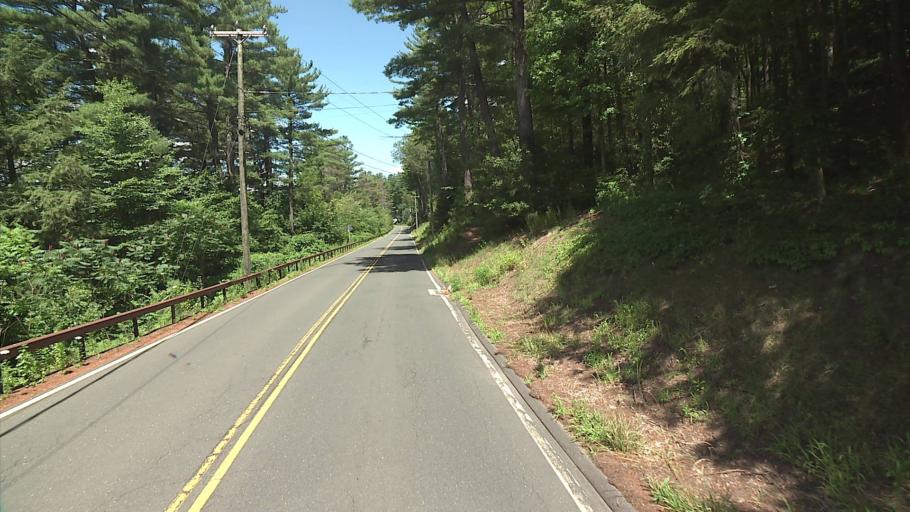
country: US
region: Connecticut
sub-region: Litchfield County
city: New Hartford Center
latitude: 41.8959
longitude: -72.9578
